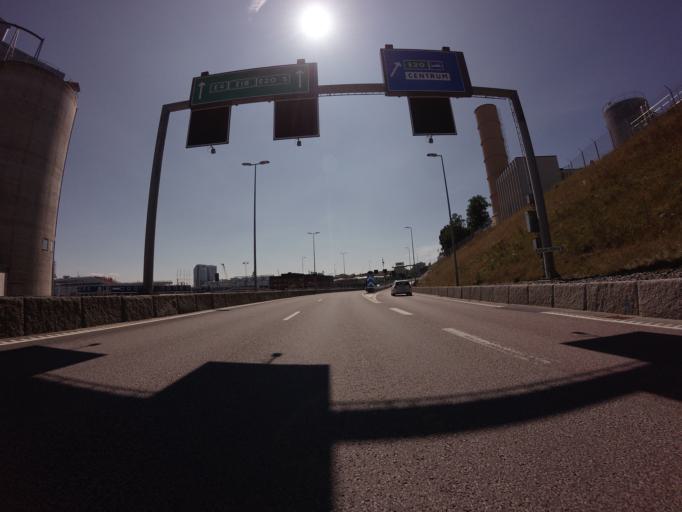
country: SE
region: Stockholm
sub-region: Stockholms Kommun
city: OEstermalm
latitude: 59.3532
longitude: 18.1065
